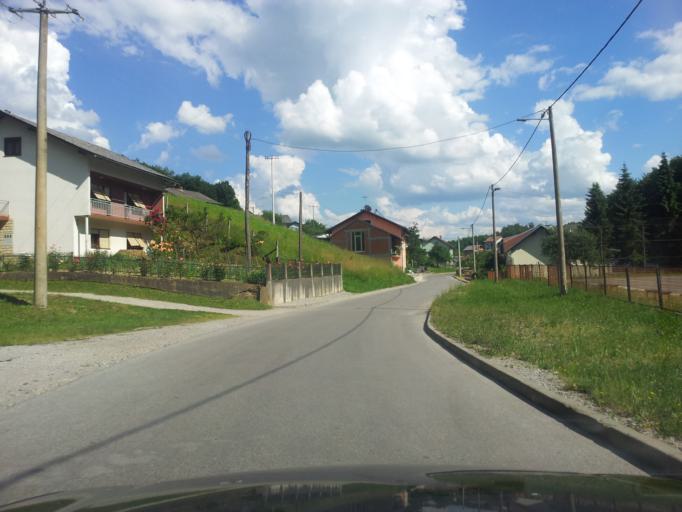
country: HR
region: Karlovacka
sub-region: Grad Karlovac
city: Karlovac
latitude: 45.4620
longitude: 15.4798
